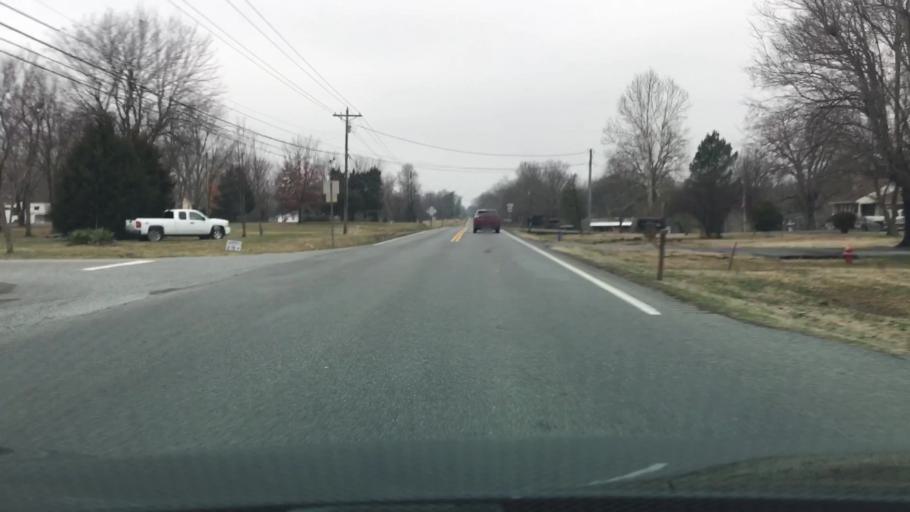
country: US
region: Kentucky
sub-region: Marshall County
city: Calvert City
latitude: 36.9734
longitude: -88.4015
